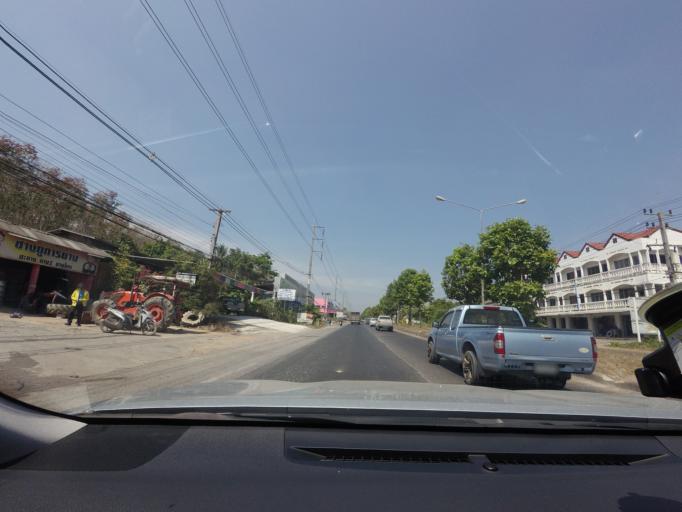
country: TH
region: Surat Thani
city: Kanchanadit
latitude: 9.1626
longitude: 99.4777
